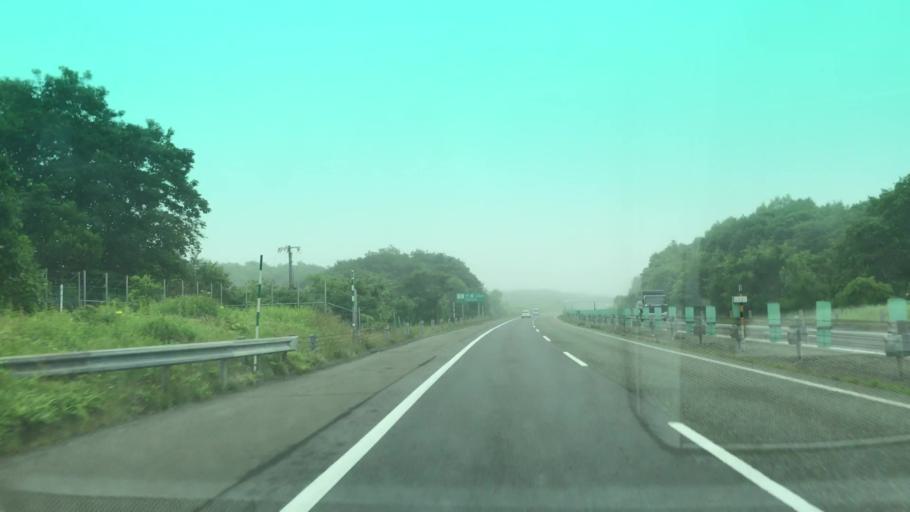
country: JP
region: Hokkaido
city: Chitose
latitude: 42.8310
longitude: 141.6118
